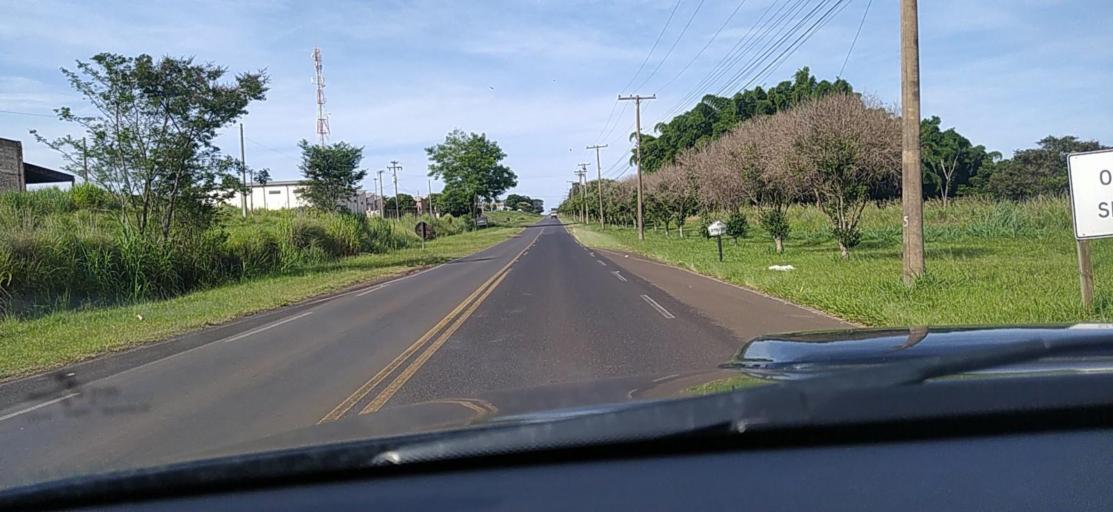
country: BR
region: Sao Paulo
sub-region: Pindorama
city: Pindorama
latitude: -21.1937
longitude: -48.9156
